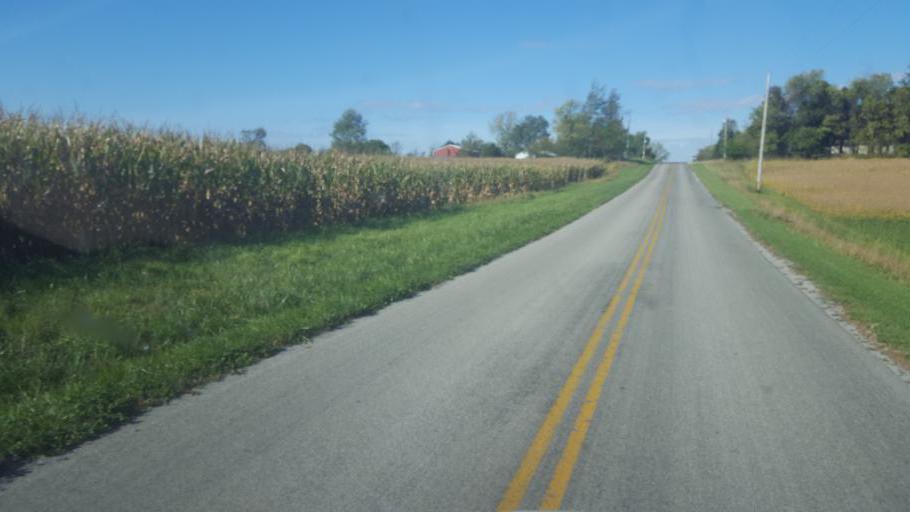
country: US
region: Ohio
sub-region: Wyandot County
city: Upper Sandusky
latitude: 40.7748
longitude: -83.2107
